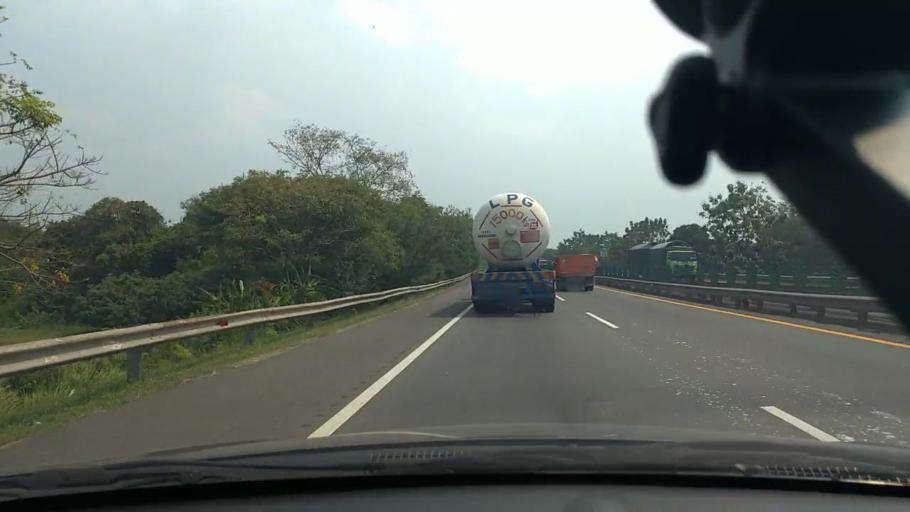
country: ID
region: Banten
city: Serang
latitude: -6.0939
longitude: 106.1610
